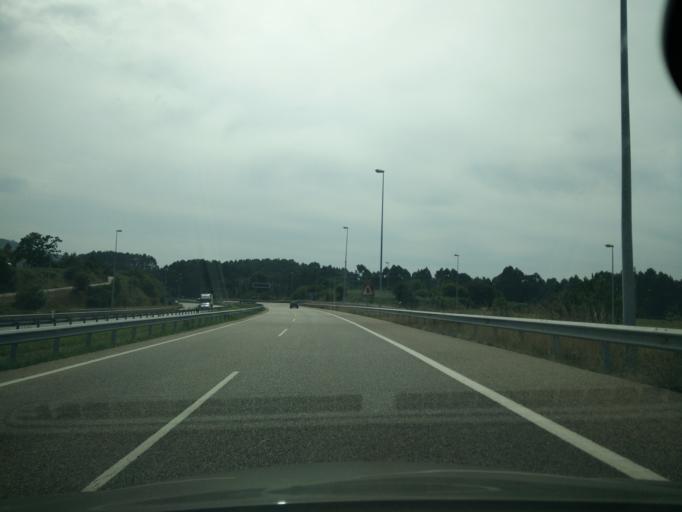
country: ES
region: Asturias
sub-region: Province of Asturias
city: Arriba
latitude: 43.5124
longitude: -5.5724
